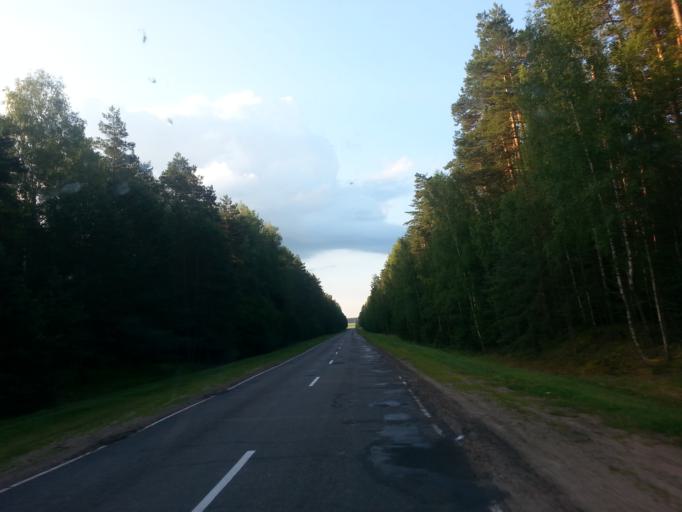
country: BY
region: Minsk
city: Il'ya
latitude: 54.4882
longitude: 27.2400
